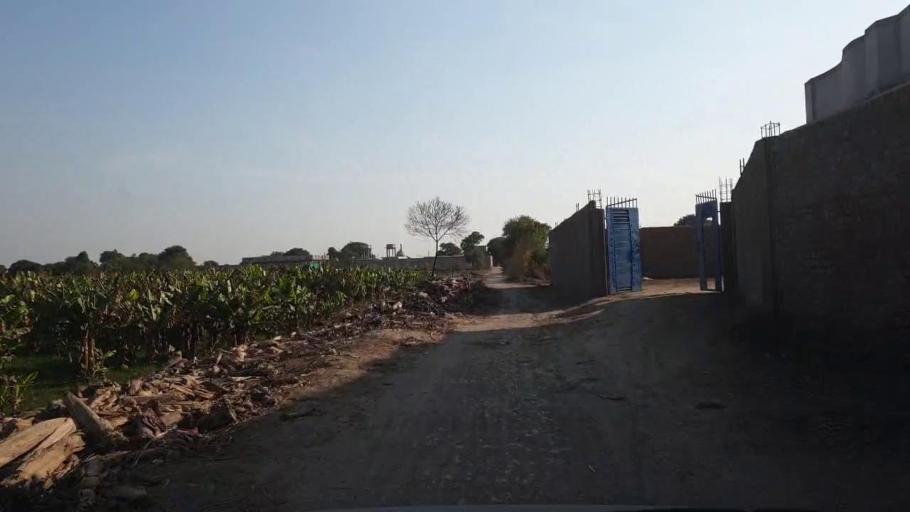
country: PK
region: Sindh
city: Chambar
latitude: 25.3109
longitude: 68.7646
